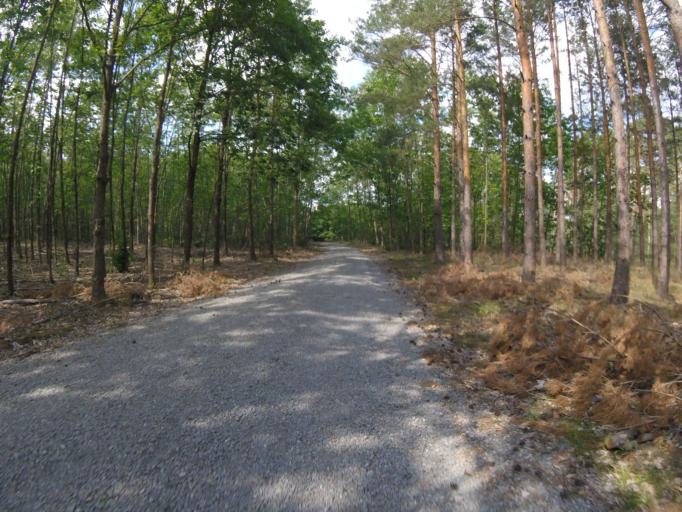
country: DE
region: Brandenburg
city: Halbe
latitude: 52.0670
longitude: 13.7813
